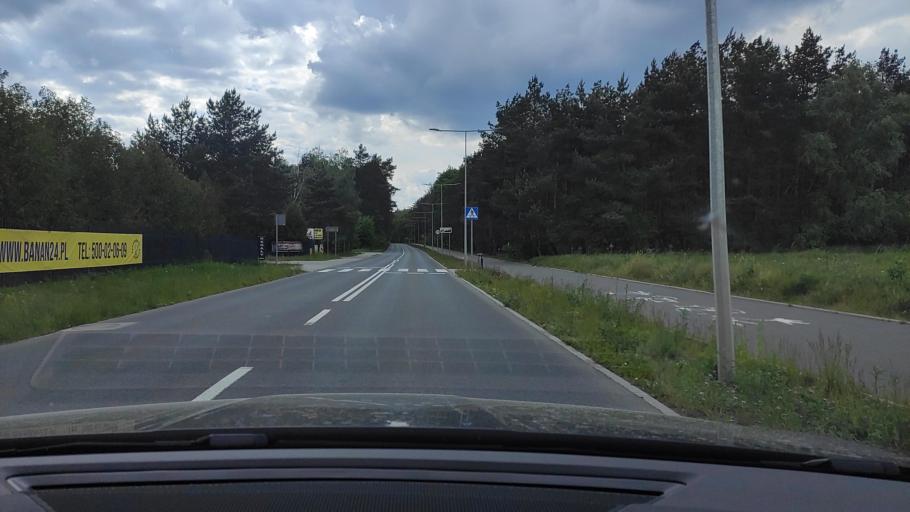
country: PL
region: Greater Poland Voivodeship
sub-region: Powiat poznanski
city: Swarzedz
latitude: 52.3844
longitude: 17.0584
